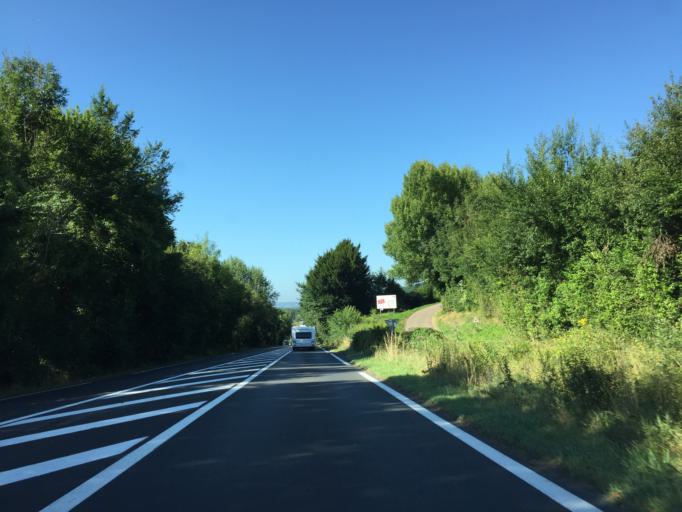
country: FR
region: Lower Normandy
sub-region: Departement du Calvados
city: Lisieux
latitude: 49.1987
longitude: 0.2269
